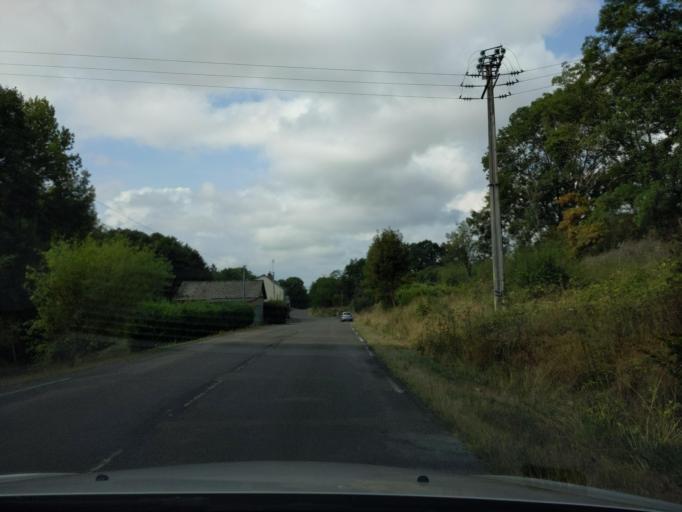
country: FR
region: Bourgogne
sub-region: Departement de Saone-et-Loire
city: Bourbon-Lancy
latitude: 46.6928
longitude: 3.8570
